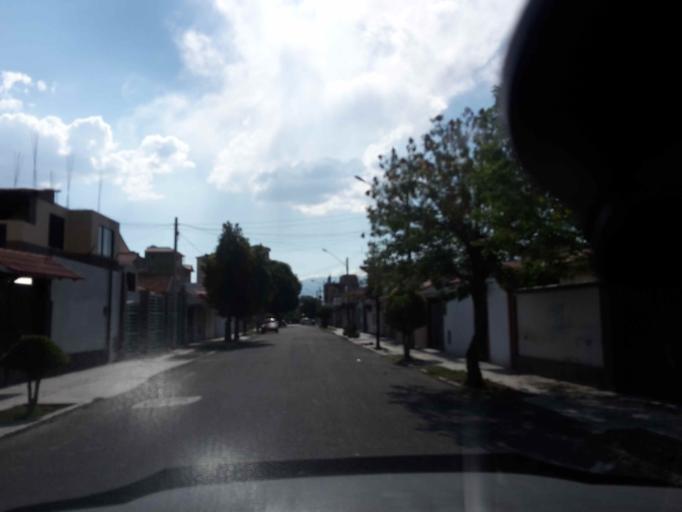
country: BO
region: Cochabamba
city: Cochabamba
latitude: -17.3704
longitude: -66.1815
